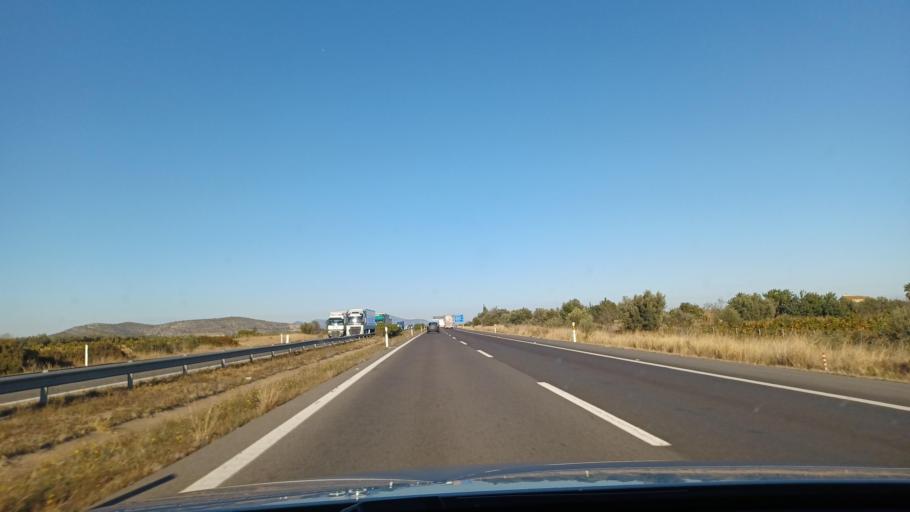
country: ES
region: Valencia
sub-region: Provincia de Castello
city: Benicarlo
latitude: 40.4462
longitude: 0.3961
